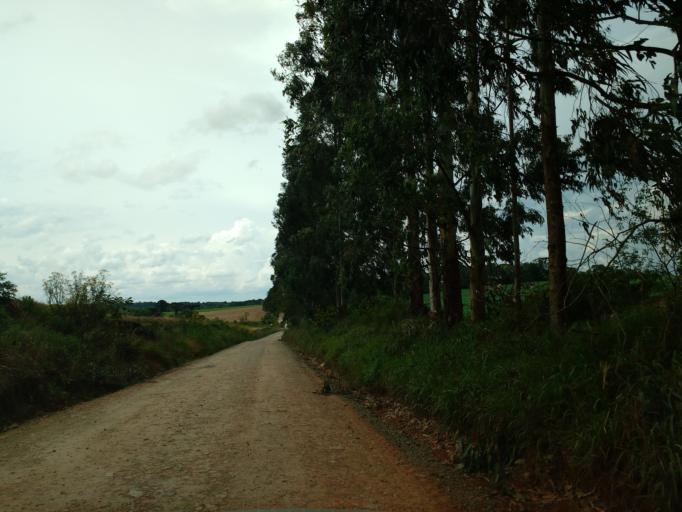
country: BR
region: Parana
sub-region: Prudentopolis
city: Prudentopolis
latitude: -25.1529
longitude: -51.0262
